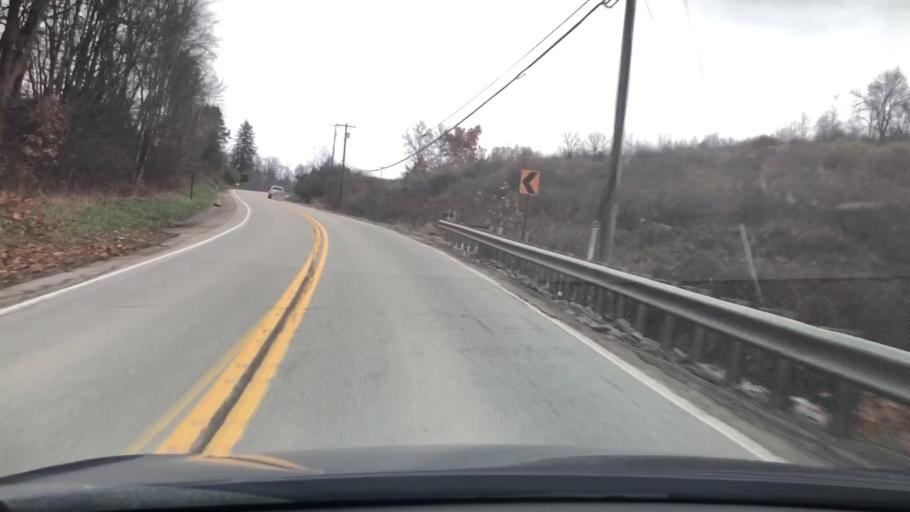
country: US
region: Pennsylvania
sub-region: Armstrong County
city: Kittanning
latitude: 40.8436
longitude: -79.4639
